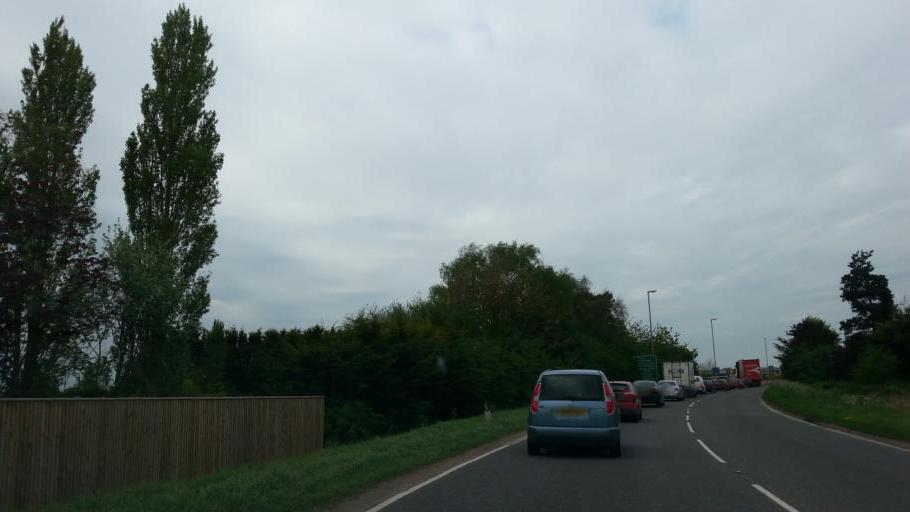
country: GB
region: England
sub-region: Cambridgeshire
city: March
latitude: 52.5572
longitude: 0.0666
